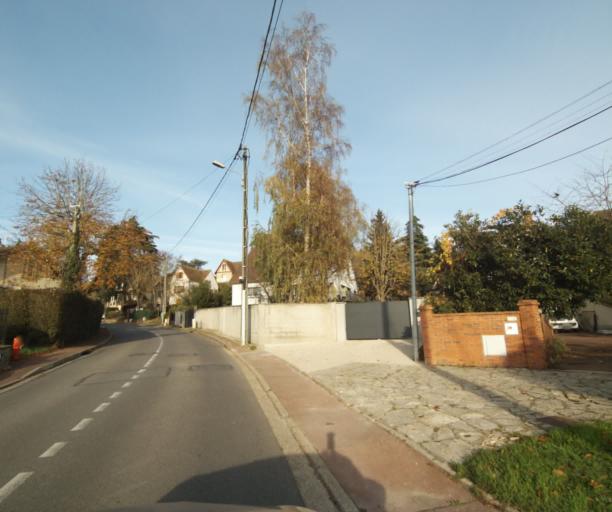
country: FR
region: Ile-de-France
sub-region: Departement des Yvelines
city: Triel-sur-Seine
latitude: 48.9868
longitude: 2.0062
